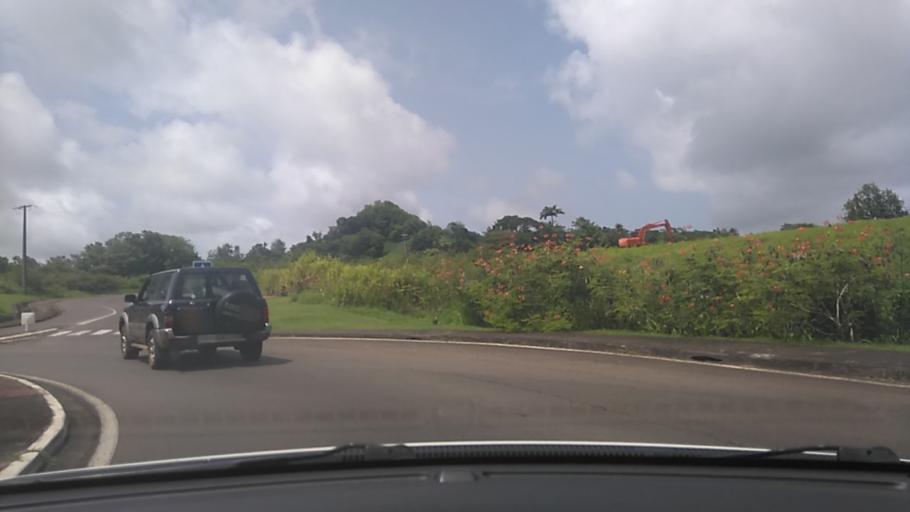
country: MQ
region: Martinique
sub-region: Martinique
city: Saint-Esprit
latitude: 14.5577
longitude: -60.9300
